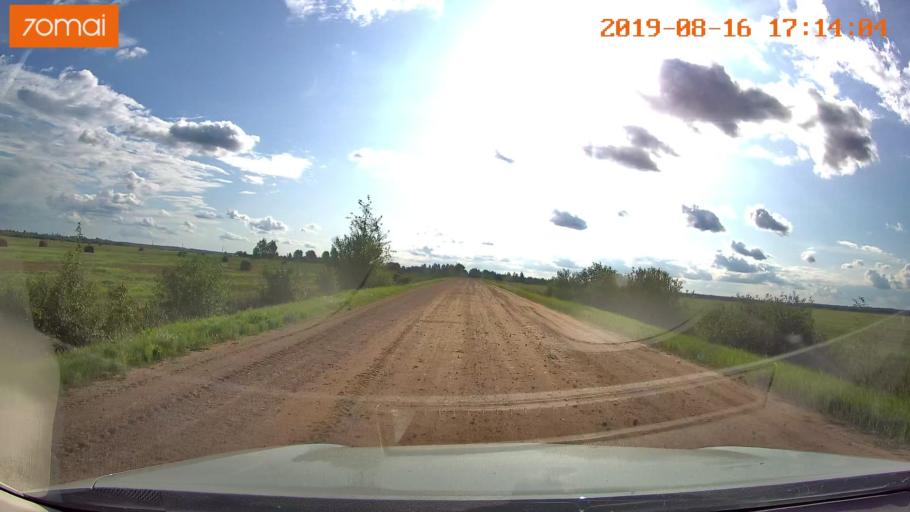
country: BY
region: Mogilev
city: Hlusha
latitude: 53.1861
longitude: 28.8650
